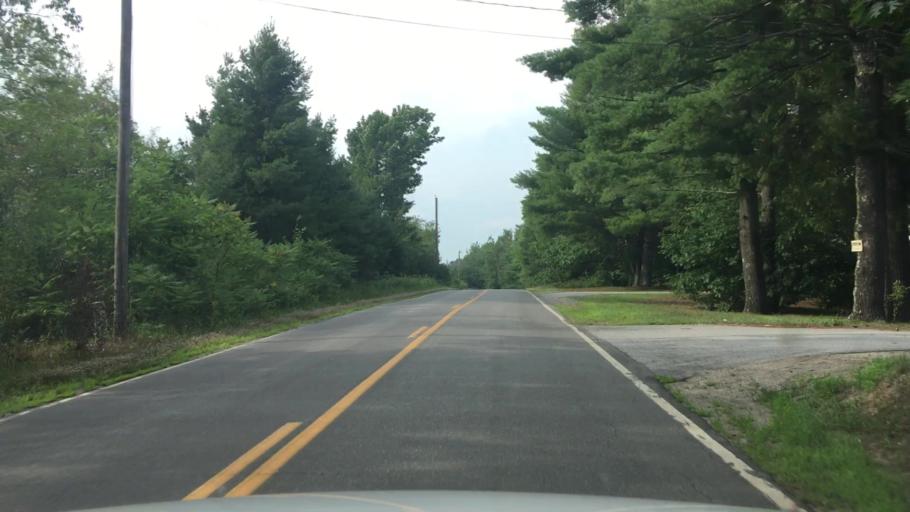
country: US
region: Maine
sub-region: Knox County
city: Washington
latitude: 44.2219
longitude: -69.3867
